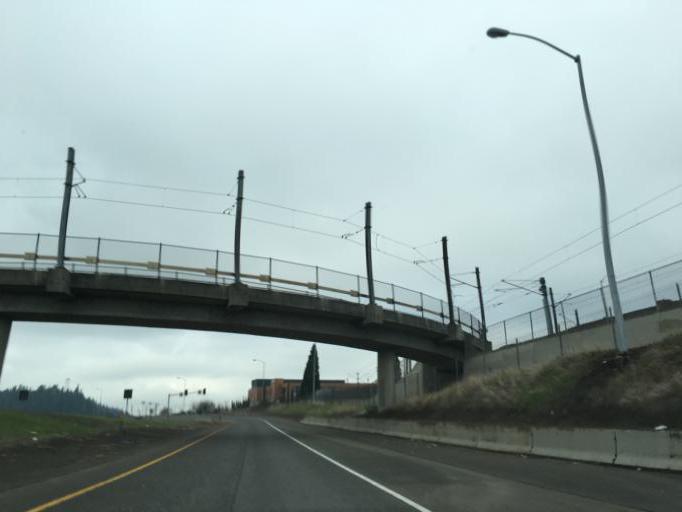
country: US
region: Oregon
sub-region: Multnomah County
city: Lents
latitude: 45.5280
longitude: -122.5643
